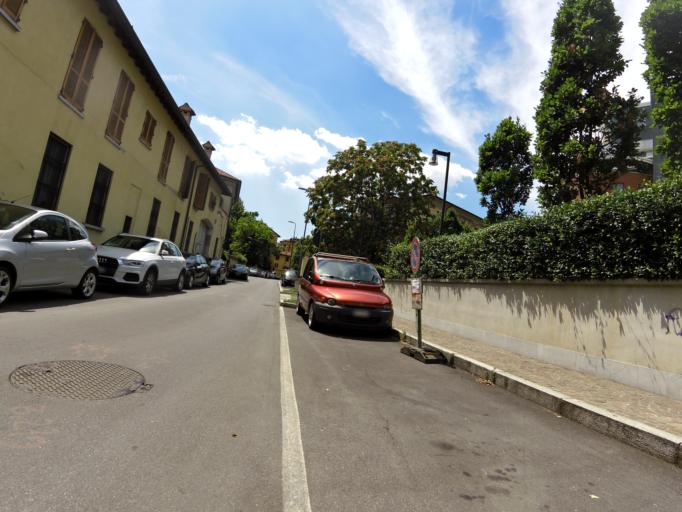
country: IT
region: Lombardy
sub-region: Citta metropolitana di Milano
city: Novegro-Tregarezzo-San Felice
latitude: 45.4857
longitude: 9.2431
